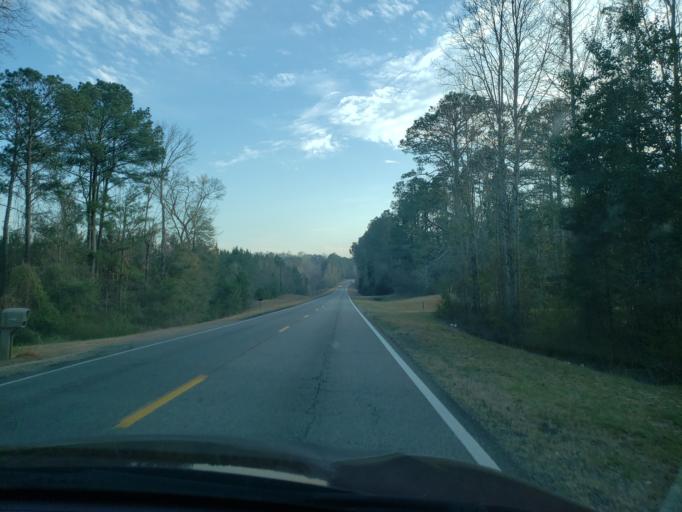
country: US
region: Alabama
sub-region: Hale County
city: Greensboro
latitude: 32.7402
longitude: -87.5856
